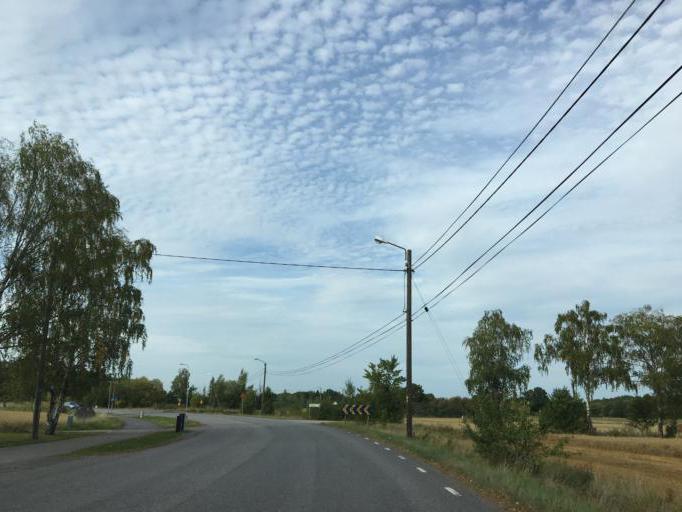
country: SE
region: Soedermanland
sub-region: Eskilstuna Kommun
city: Torshalla
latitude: 59.4337
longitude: 16.4754
